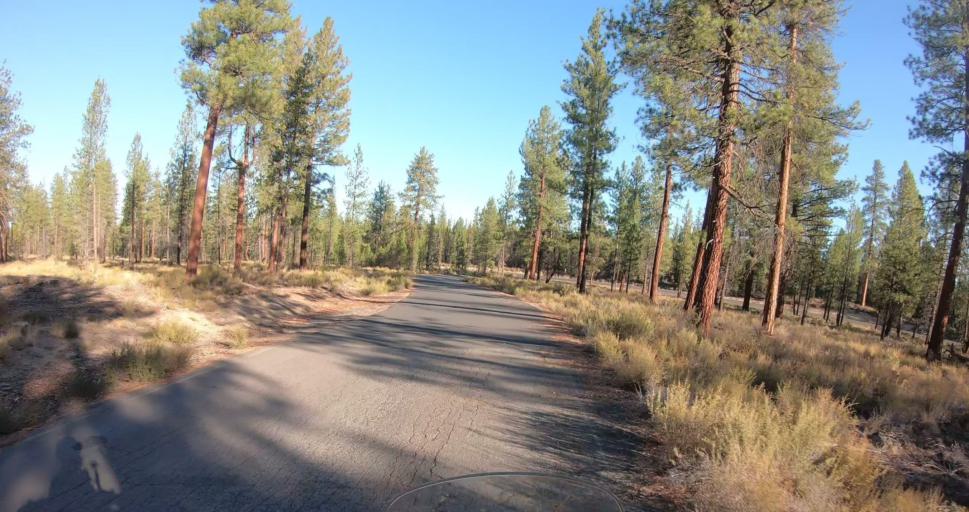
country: US
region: Oregon
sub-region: Deschutes County
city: La Pine
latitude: 43.7257
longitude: -121.4187
